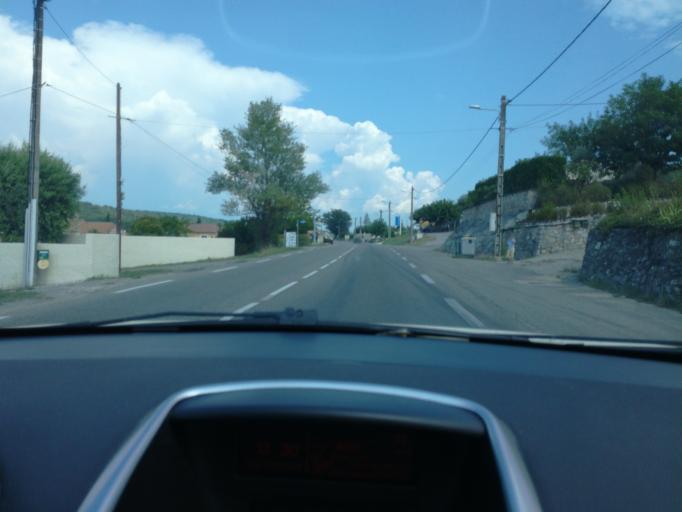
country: FR
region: Rhone-Alpes
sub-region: Departement de l'Ardeche
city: Ruoms
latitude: 44.4626
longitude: 4.3445
